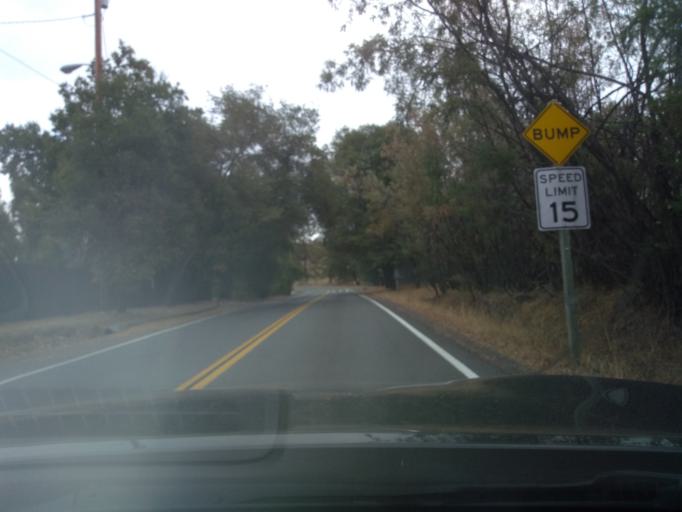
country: US
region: California
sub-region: Mendocino County
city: Ukiah
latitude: 39.1988
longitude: -123.1870
